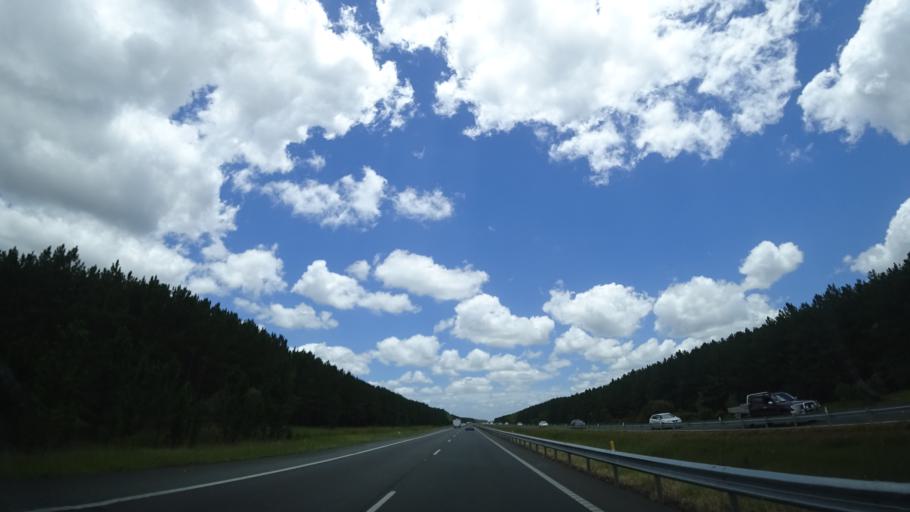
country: AU
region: Queensland
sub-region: Sunshine Coast
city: Little Mountain
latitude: -26.8821
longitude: 153.0071
